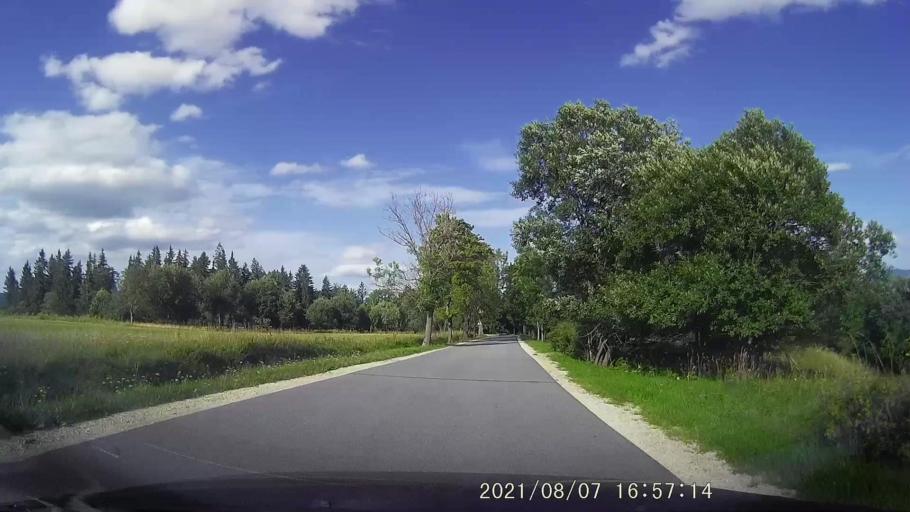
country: PL
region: Lower Silesian Voivodeship
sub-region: Powiat klodzki
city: Bystrzyca Klodzka
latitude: 50.2819
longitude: 16.5432
